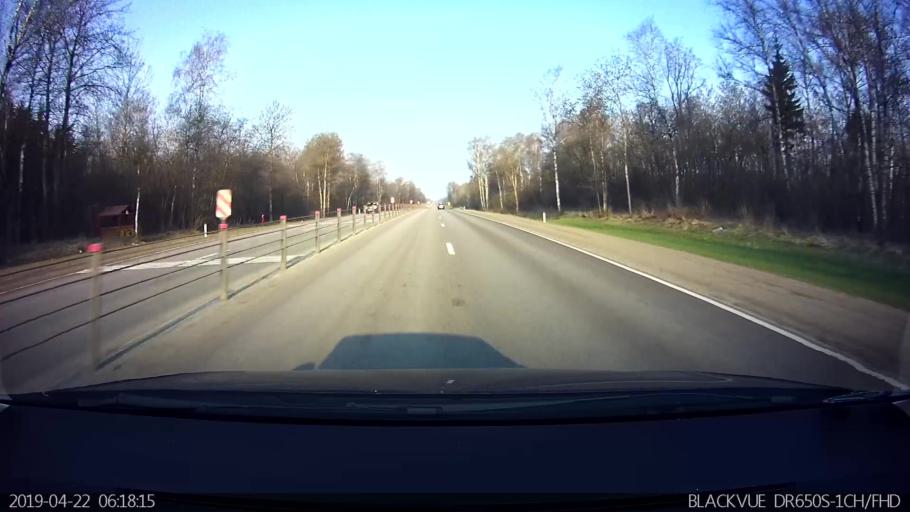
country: RU
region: Moskovskaya
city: Mozhaysk
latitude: 55.4629
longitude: 35.9655
